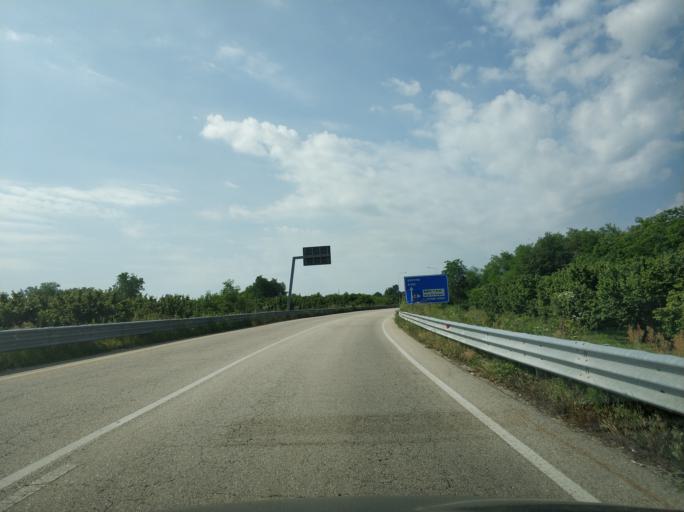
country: IT
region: Piedmont
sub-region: Provincia di Cuneo
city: Monta
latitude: 44.8193
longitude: 7.9482
